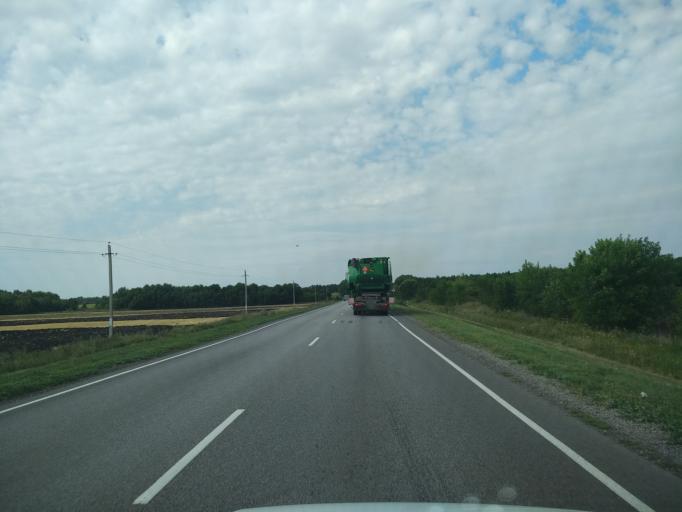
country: RU
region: Voronezj
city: Pereleshinskiy
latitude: 51.8802
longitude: 40.4184
